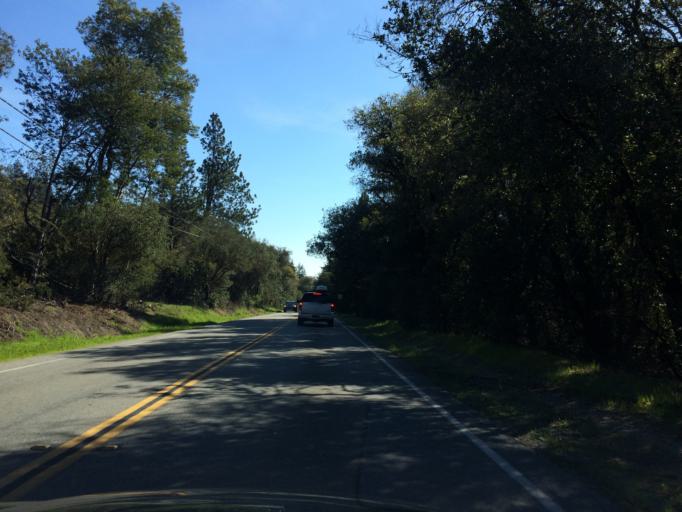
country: US
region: California
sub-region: Santa Cruz County
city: Pasatiempo
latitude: 37.0288
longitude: -122.0397
